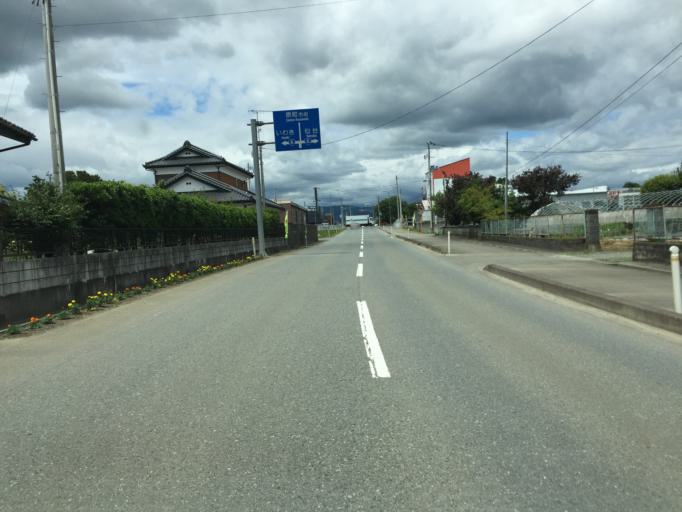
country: JP
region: Fukushima
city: Namie
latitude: 37.6468
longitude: 140.9868
